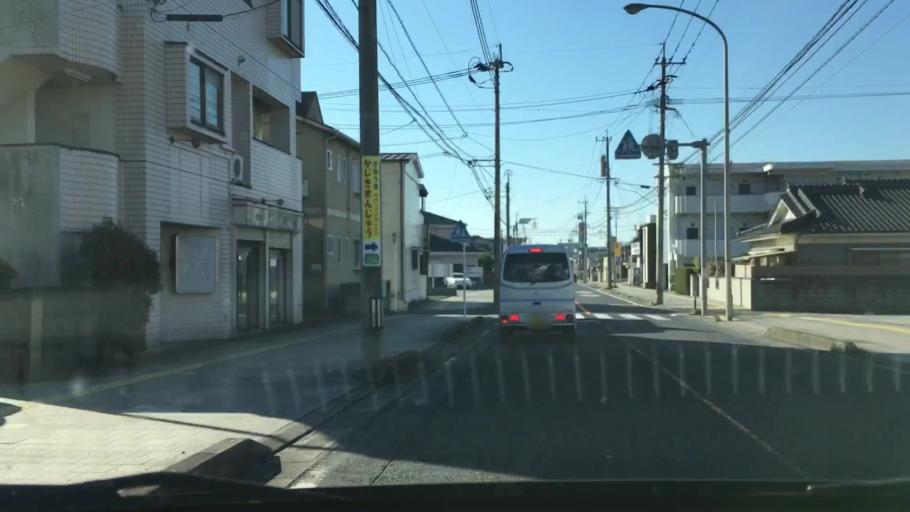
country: JP
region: Kagoshima
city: Kajiki
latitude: 31.7428
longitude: 130.6688
